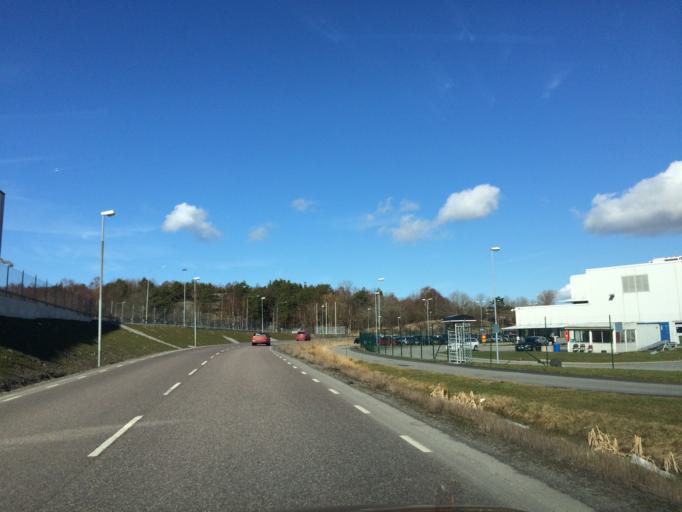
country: SE
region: Vaestra Goetaland
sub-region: Goteborg
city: Torslanda
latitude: 57.7141
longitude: 11.8161
